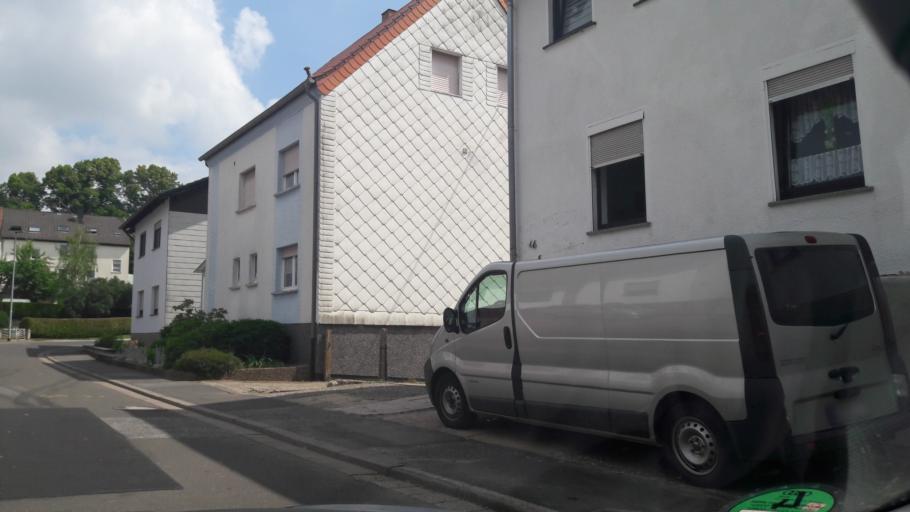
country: DE
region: Saarland
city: Namborn
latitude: 49.4953
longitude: 7.1198
